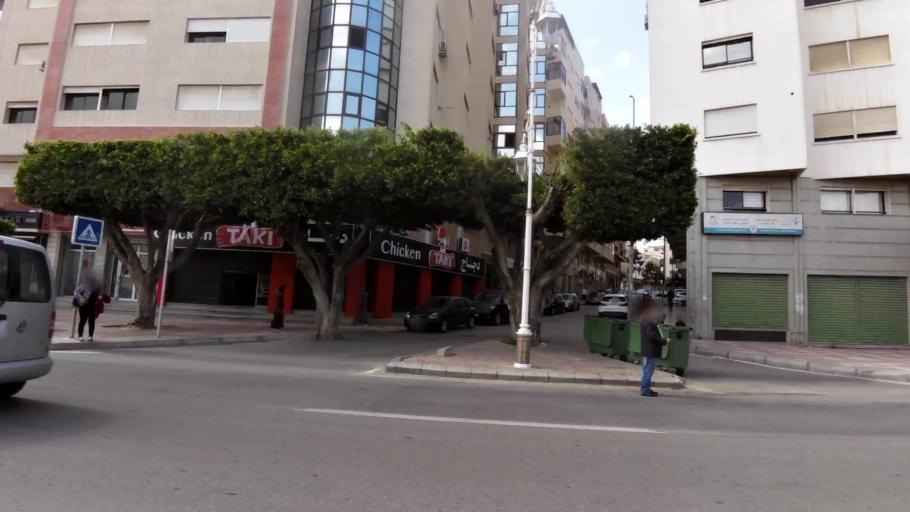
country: MA
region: Tanger-Tetouan
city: Tetouan
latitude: 35.5834
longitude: -5.3505
